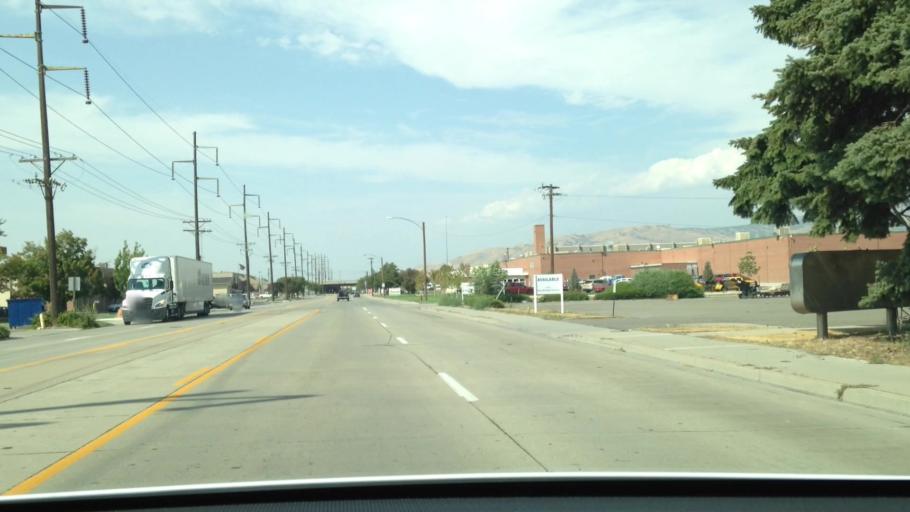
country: US
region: Utah
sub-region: Salt Lake County
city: South Salt Lake
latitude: 40.7176
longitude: -111.9174
